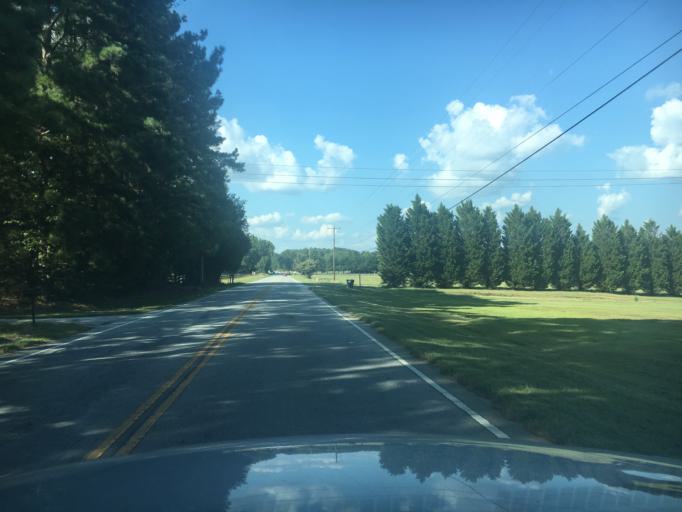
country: US
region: South Carolina
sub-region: Greenville County
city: Fountain Inn
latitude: 34.6498
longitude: -82.2574
